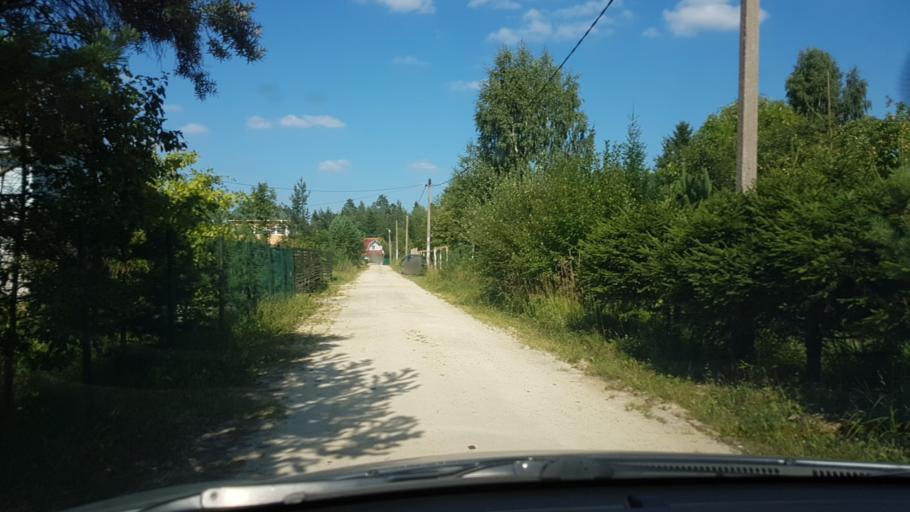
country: RU
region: Leningrad
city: Vyritsa
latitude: 59.4531
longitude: 30.3018
